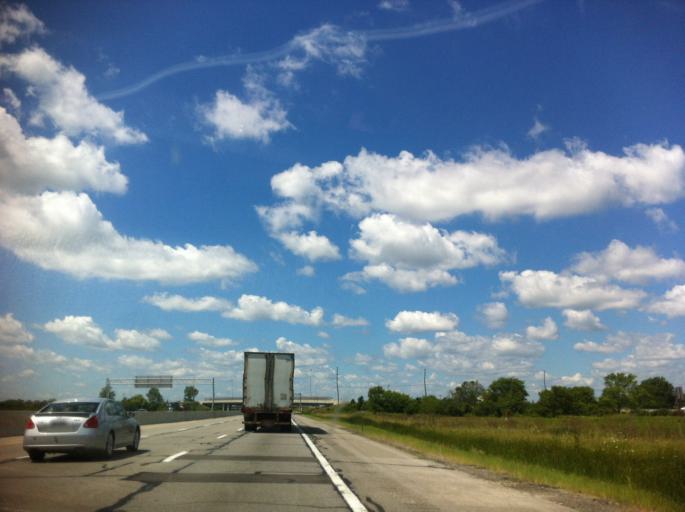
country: US
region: Ohio
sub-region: Wood County
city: Rossford
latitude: 41.5628
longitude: -83.5679
